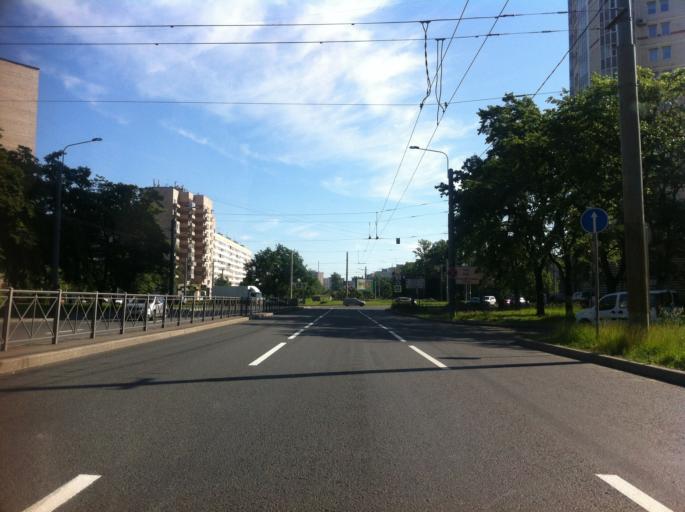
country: RU
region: St.-Petersburg
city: Dachnoye
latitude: 59.8436
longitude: 30.2476
